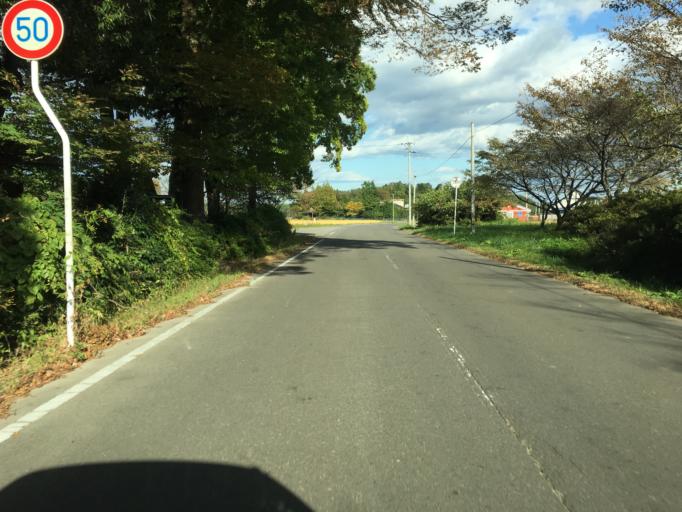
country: JP
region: Miyagi
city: Marumori
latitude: 37.8614
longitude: 140.8834
